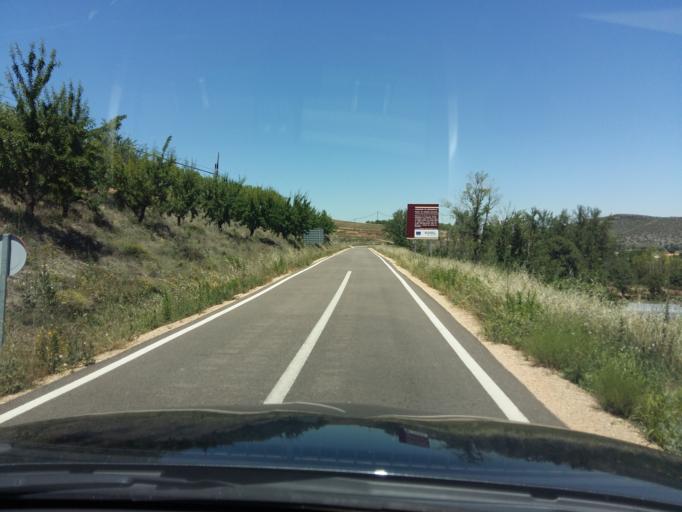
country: ES
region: Aragon
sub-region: Provincia de Zaragoza
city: Alcala de Moncayo
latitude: 41.7910
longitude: -1.6996
